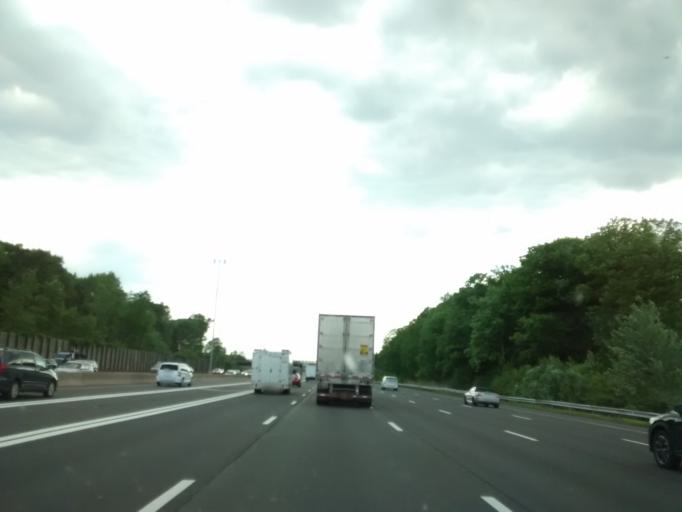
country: US
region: Connecticut
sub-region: Hartford County
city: East Hartford
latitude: 41.7689
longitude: -72.6142
